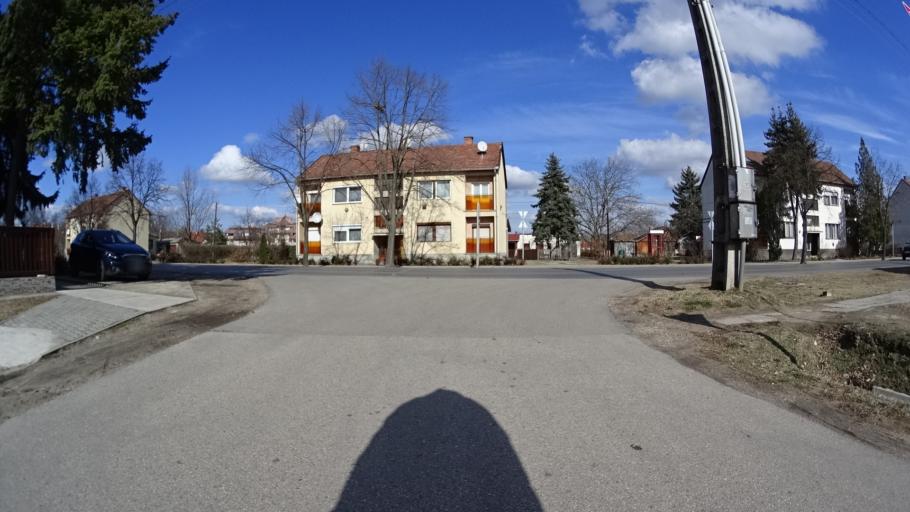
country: HU
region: Bacs-Kiskun
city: Tiszakecske
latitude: 46.9382
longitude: 20.0986
